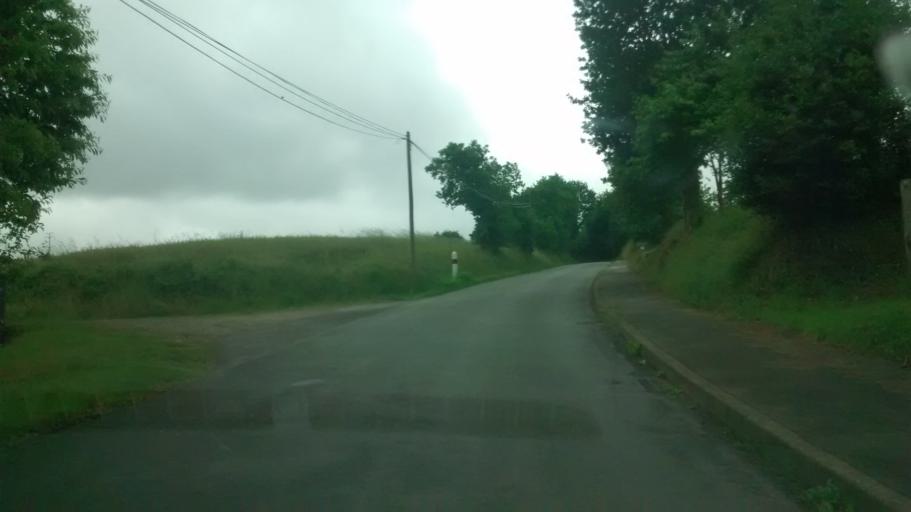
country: FR
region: Brittany
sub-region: Departement du Morbihan
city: Serent
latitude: 47.8179
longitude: -2.5029
